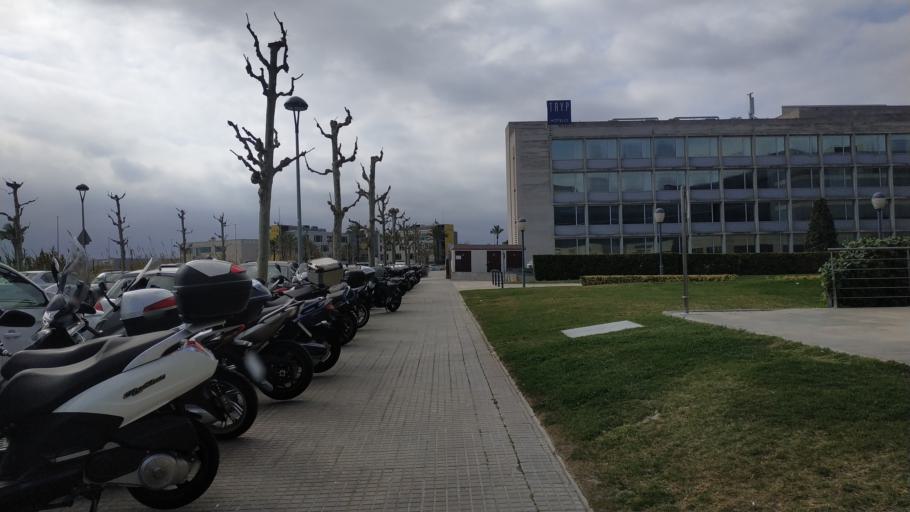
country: ES
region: Catalonia
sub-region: Provincia de Barcelona
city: El Prat de Llobregat
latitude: 41.3132
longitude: 2.0695
